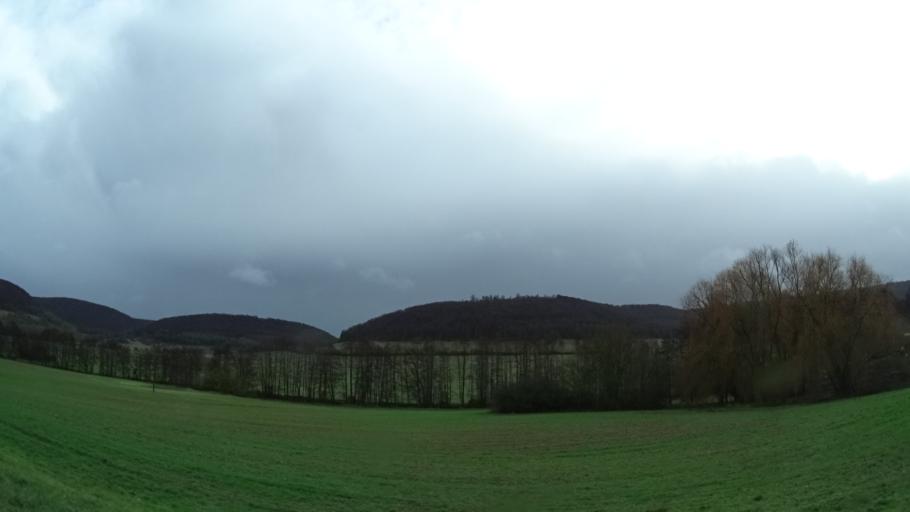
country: DE
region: Thuringia
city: Stepfershausen
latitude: 50.5704
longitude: 10.3227
